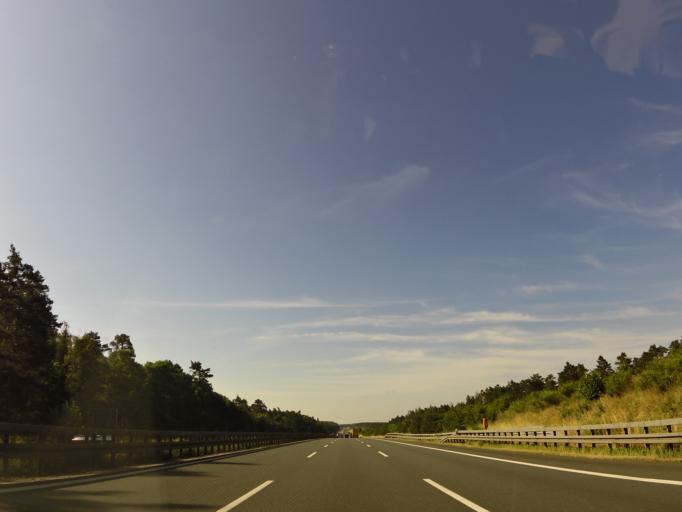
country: DE
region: Bavaria
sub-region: Regierungsbezirk Mittelfranken
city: Allersberg
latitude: 49.3017
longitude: 11.2080
